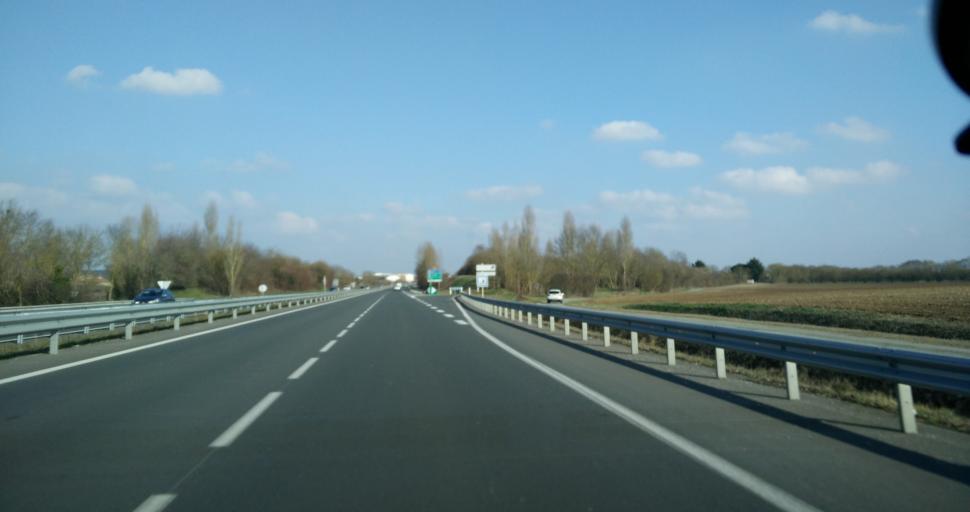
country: FR
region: Poitou-Charentes
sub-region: Departement de la Charente-Maritime
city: Sainte-Soulle
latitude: 46.2034
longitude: -1.0220
